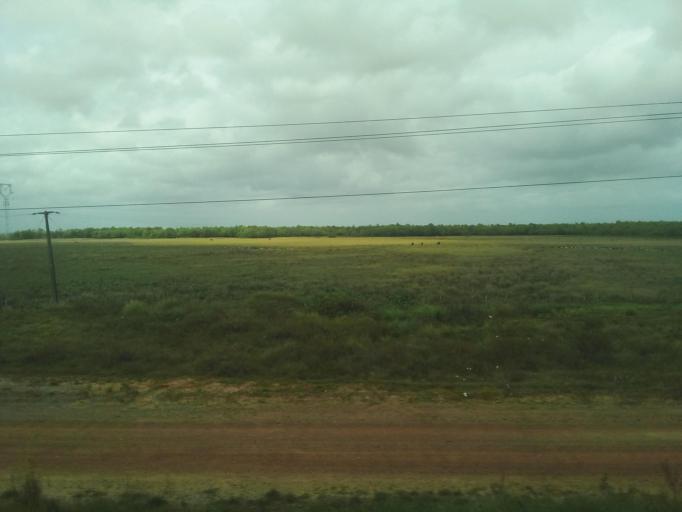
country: BR
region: Maranhao
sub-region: Icatu
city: Icatu
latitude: -2.9127
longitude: -44.3555
